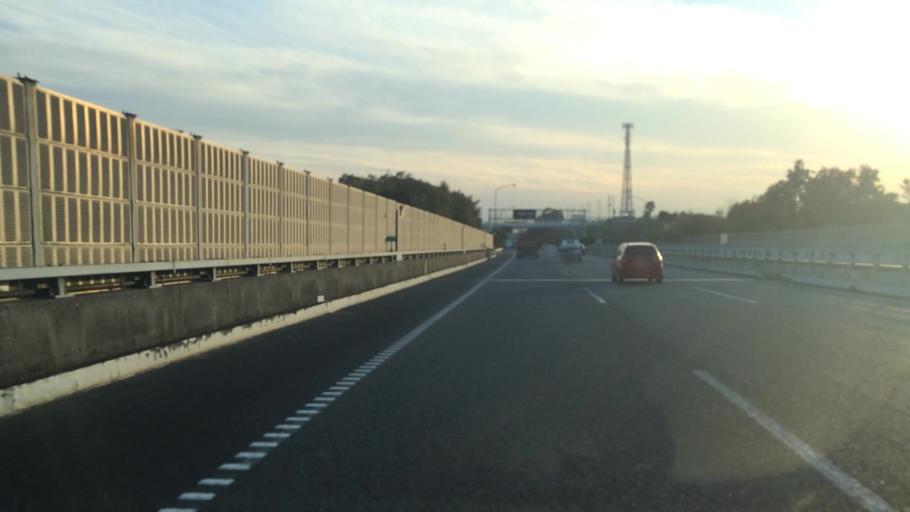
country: JP
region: Kanagawa
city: Yokohama
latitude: 35.5290
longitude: 139.5976
